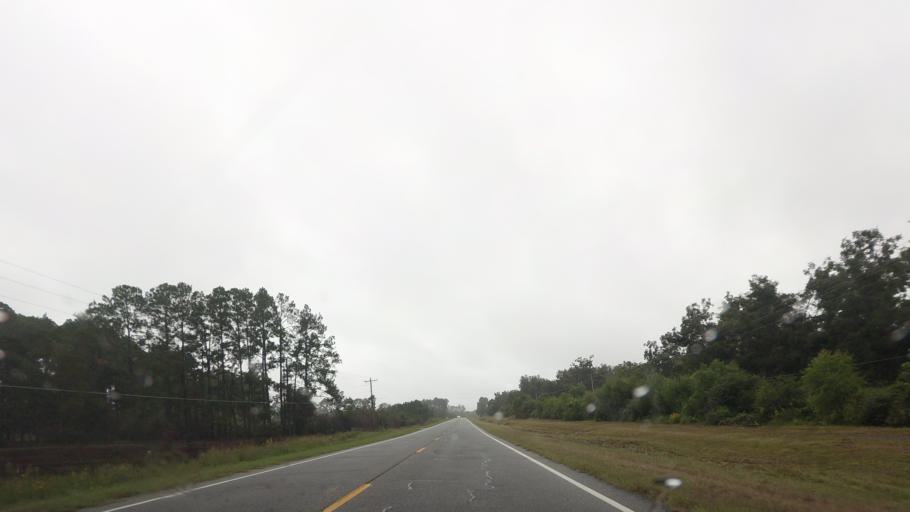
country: US
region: Georgia
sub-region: Ben Hill County
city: Fitzgerald
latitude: 31.7613
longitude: -83.2455
